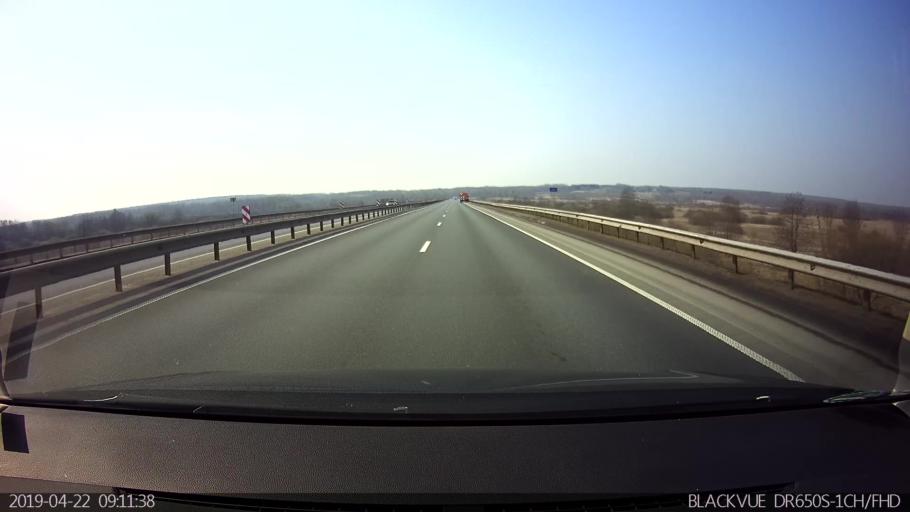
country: RU
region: Smolensk
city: Katyn'
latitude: 54.8225
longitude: 31.6472
